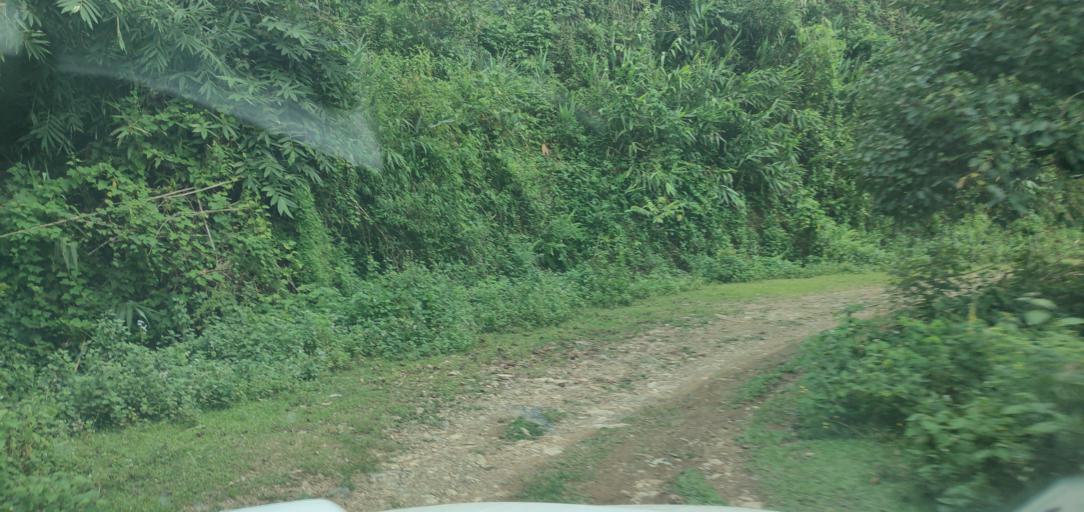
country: LA
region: Phongsali
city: Phongsali
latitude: 21.4418
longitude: 102.3276
